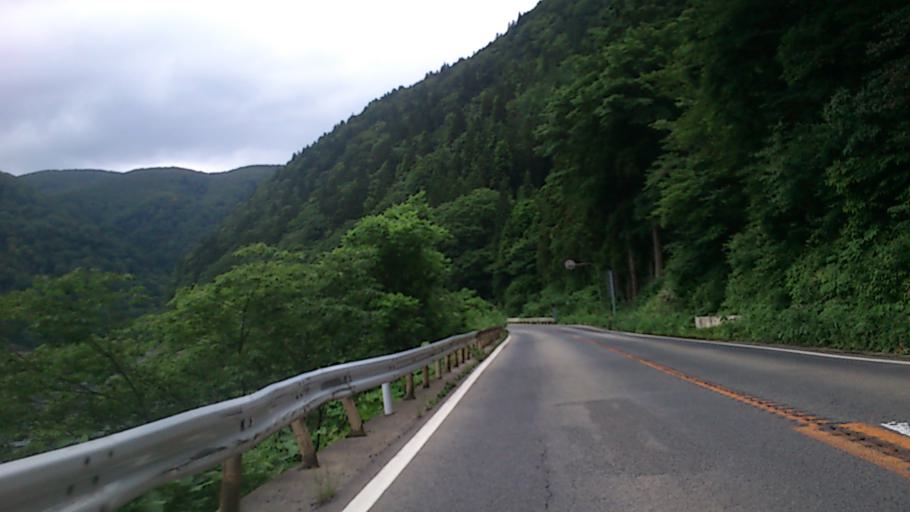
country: JP
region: Yamagata
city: Shinjo
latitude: 38.7495
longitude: 140.0826
